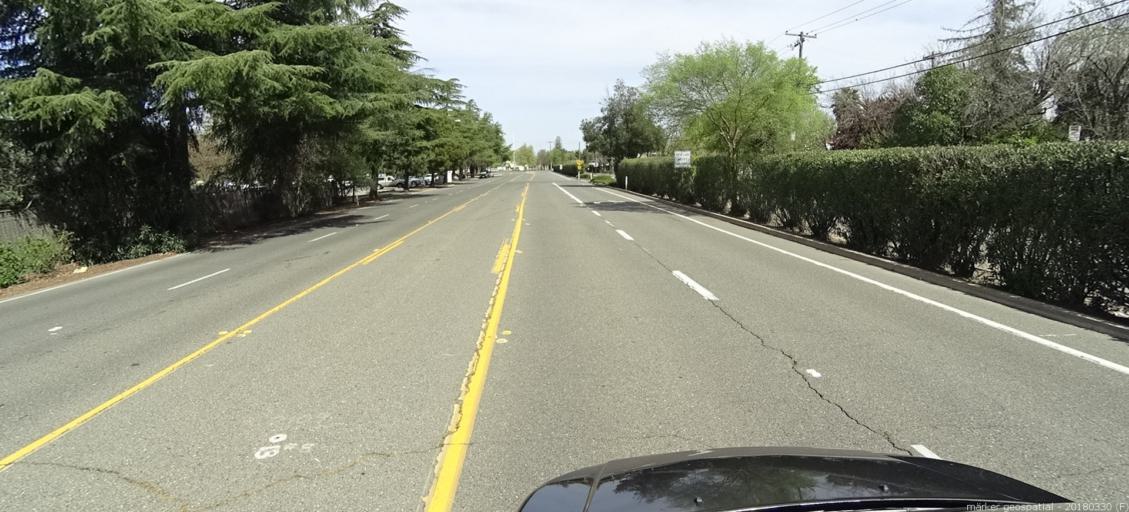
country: US
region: California
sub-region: Sacramento County
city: Rosemont
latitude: 38.5516
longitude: -121.3722
